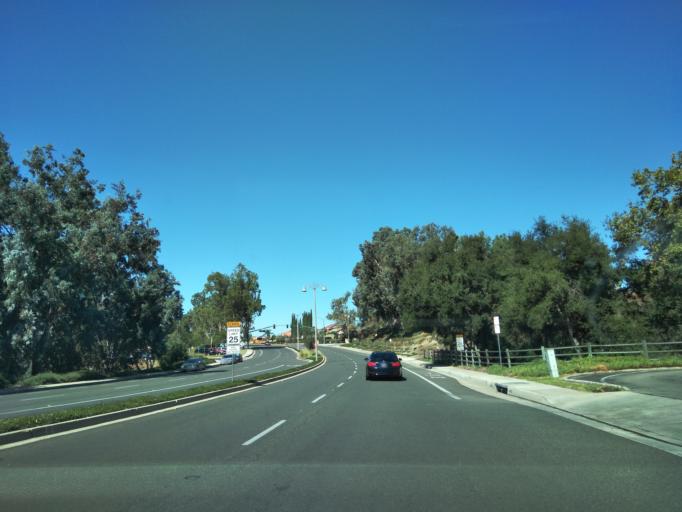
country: US
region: California
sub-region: Orange County
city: Lake Forest
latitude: 33.6292
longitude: -117.6657
